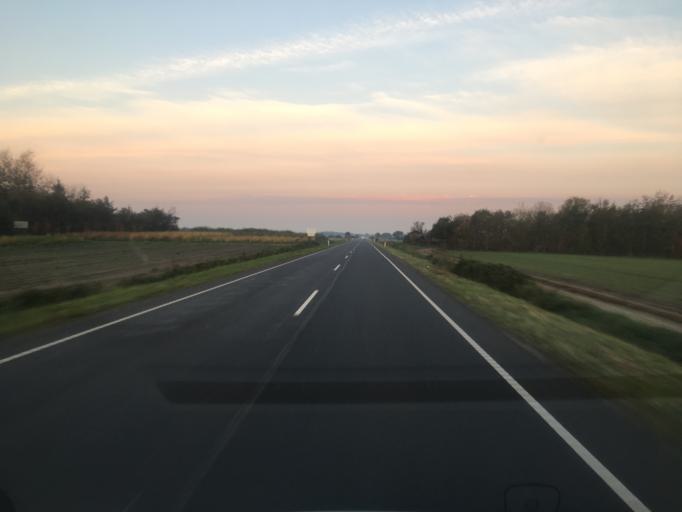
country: DE
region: Schleswig-Holstein
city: Bramstedtlund
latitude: 54.9718
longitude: 9.0802
